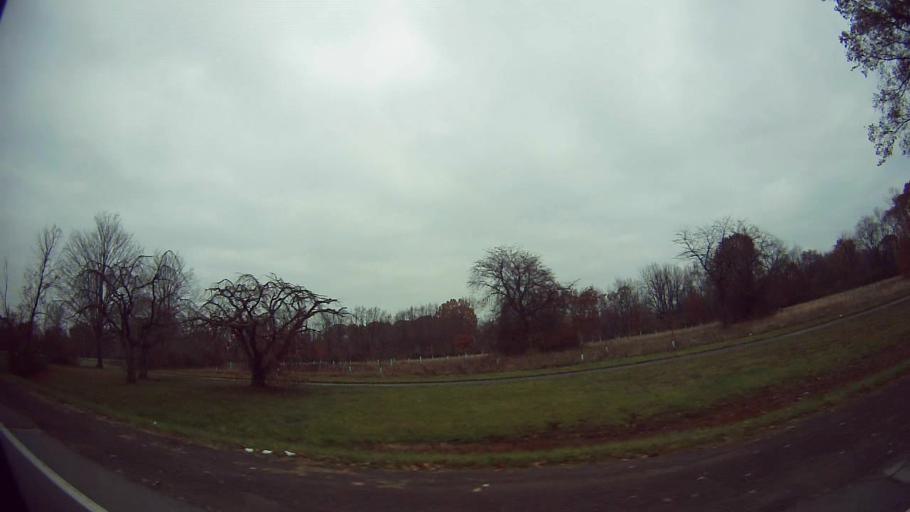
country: US
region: Michigan
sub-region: Wayne County
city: Dearborn Heights
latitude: 42.3583
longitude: -83.2630
